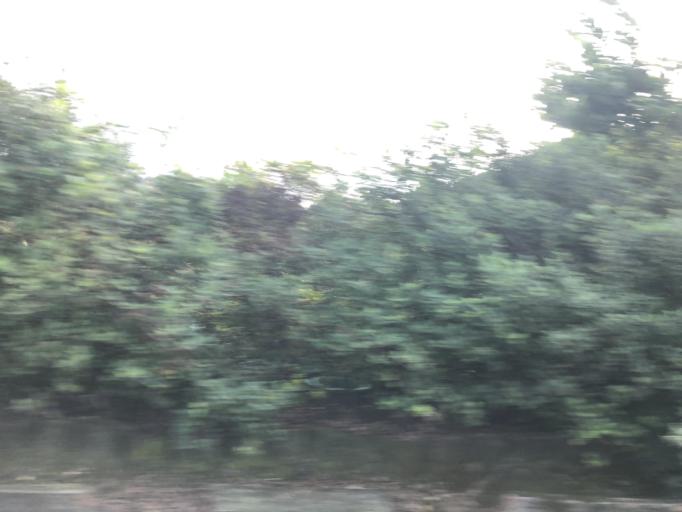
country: TW
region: Taiwan
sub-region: Keelung
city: Keelung
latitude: 25.2067
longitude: 121.6474
